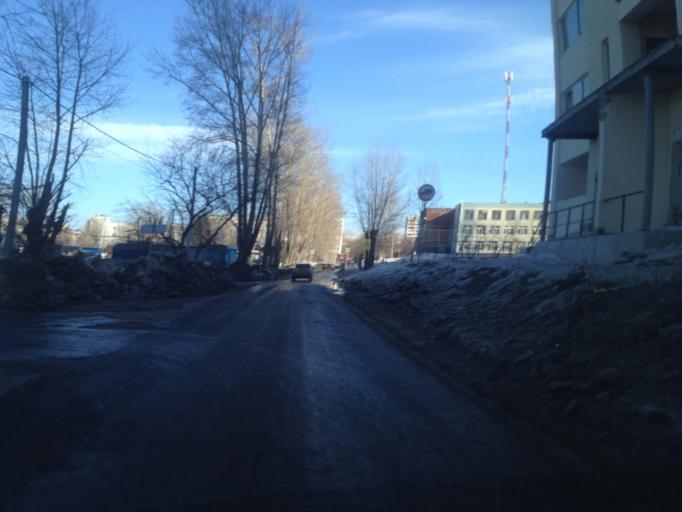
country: RU
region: Sverdlovsk
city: Shirokaya Rechka
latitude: 56.8308
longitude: 60.5303
